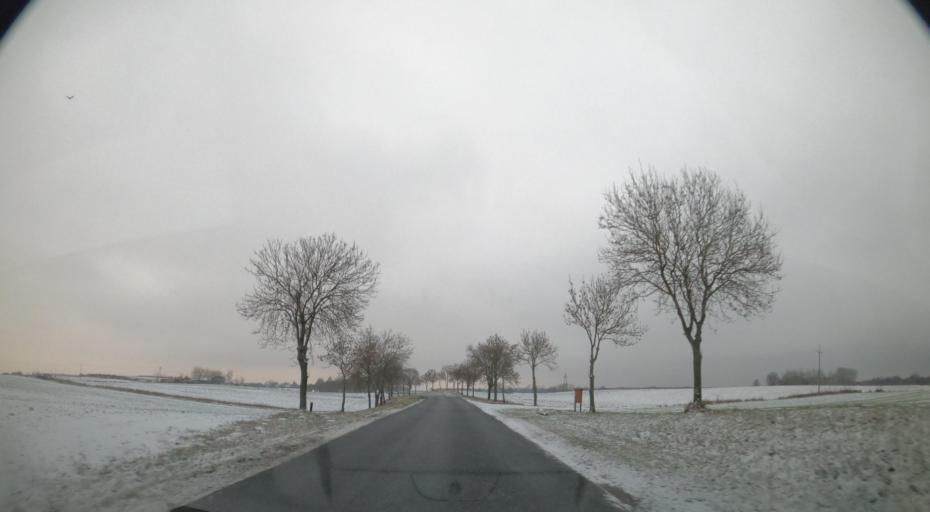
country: PL
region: Kujawsko-Pomorskie
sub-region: Powiat lipnowski
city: Wielgie
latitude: 52.7298
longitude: 19.2806
